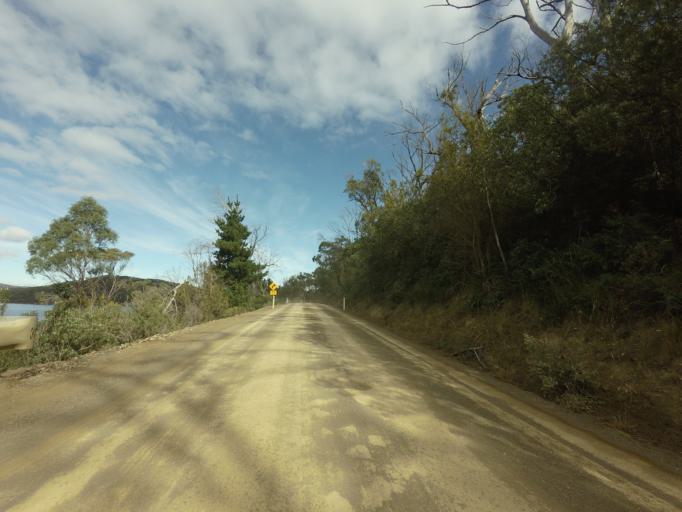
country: AU
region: Tasmania
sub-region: Clarence
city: Sandford
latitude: -43.0924
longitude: 147.7311
